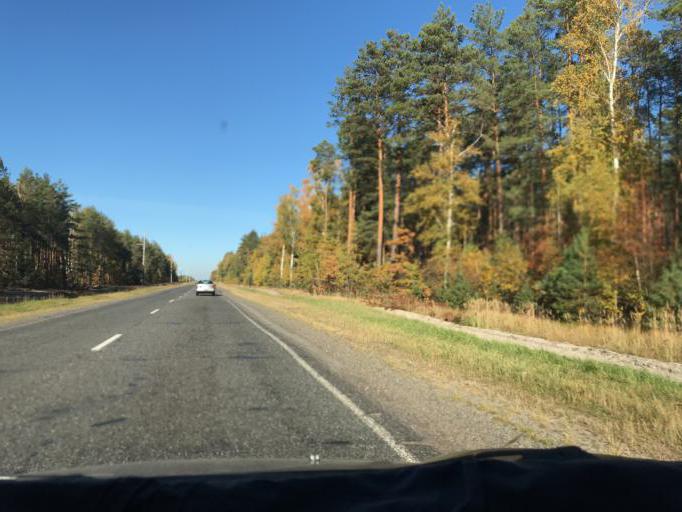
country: BY
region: Gomel
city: Yel'sk
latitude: 51.8791
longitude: 29.2363
